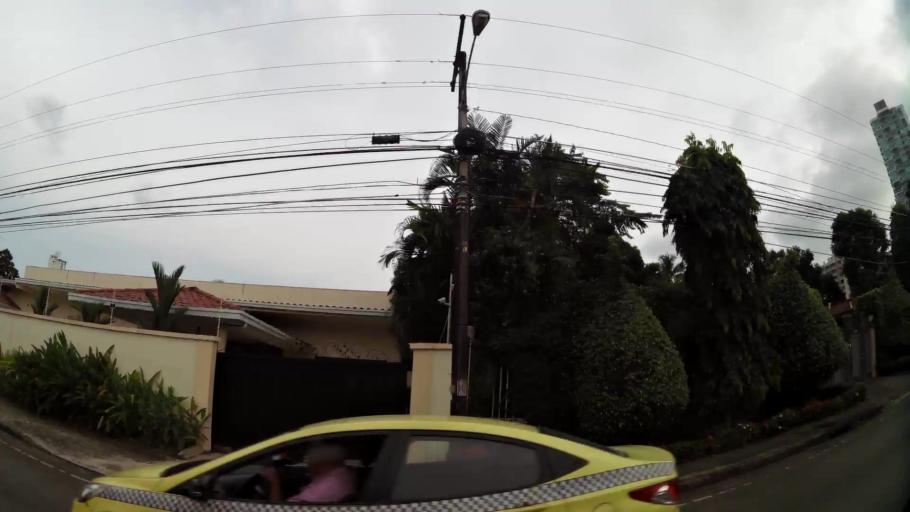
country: PA
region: Panama
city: Panama
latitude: 8.9984
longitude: -79.5028
